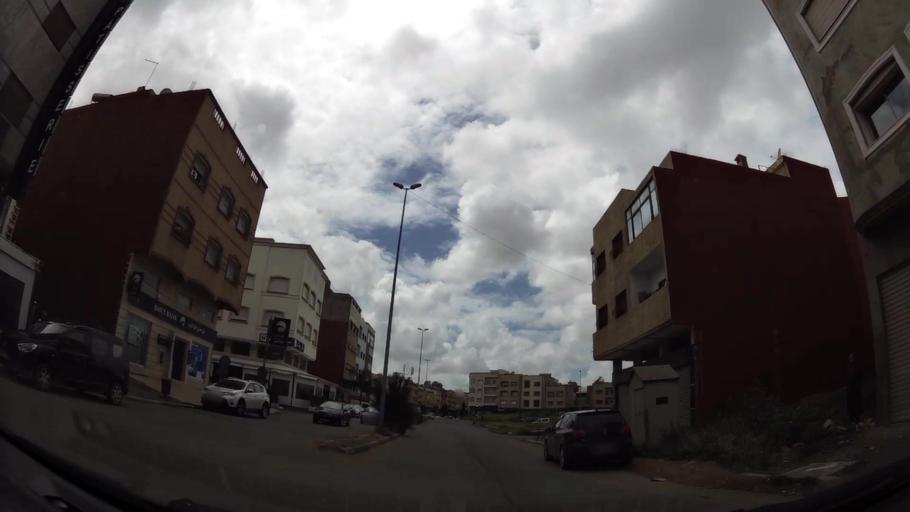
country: MA
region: Grand Casablanca
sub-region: Casablanca
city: Casablanca
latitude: 33.5367
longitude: -7.5958
